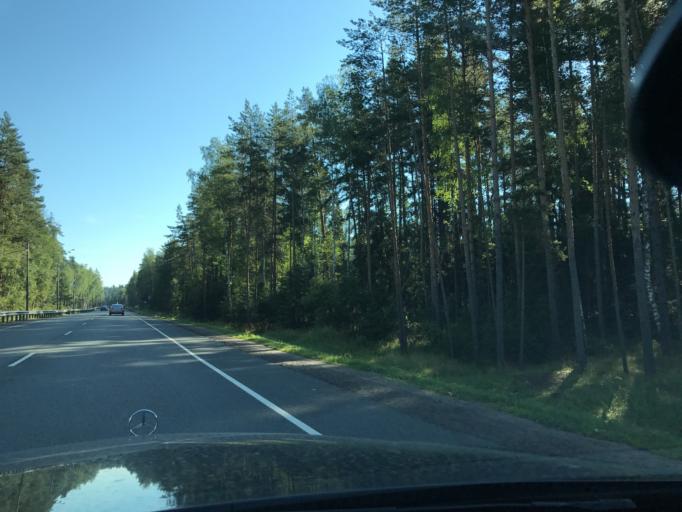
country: RU
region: Moskovskaya
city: Chernogolovka
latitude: 55.9676
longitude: 38.2882
